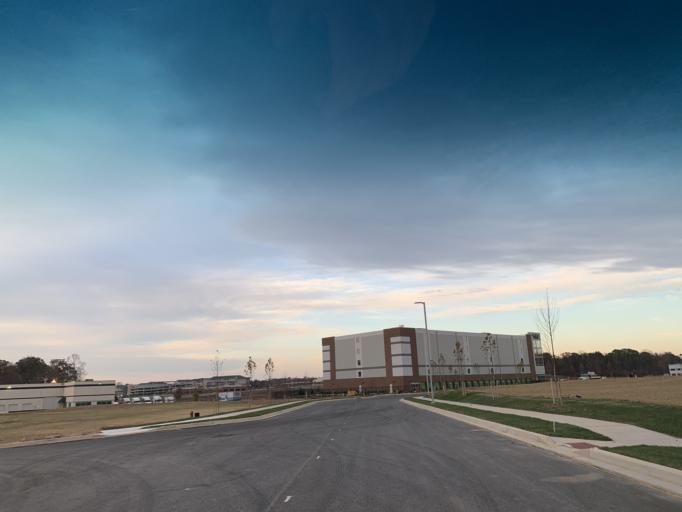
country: US
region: Maryland
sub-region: Baltimore County
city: Bowleys Quarters
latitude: 39.3487
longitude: -76.4139
